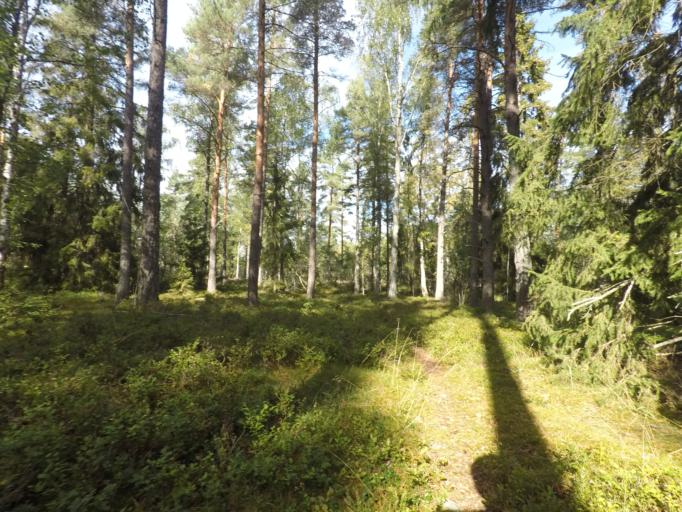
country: SE
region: Soedermanland
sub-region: Eskilstuna Kommun
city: Hallbybrunn
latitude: 59.4282
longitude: 16.4117
